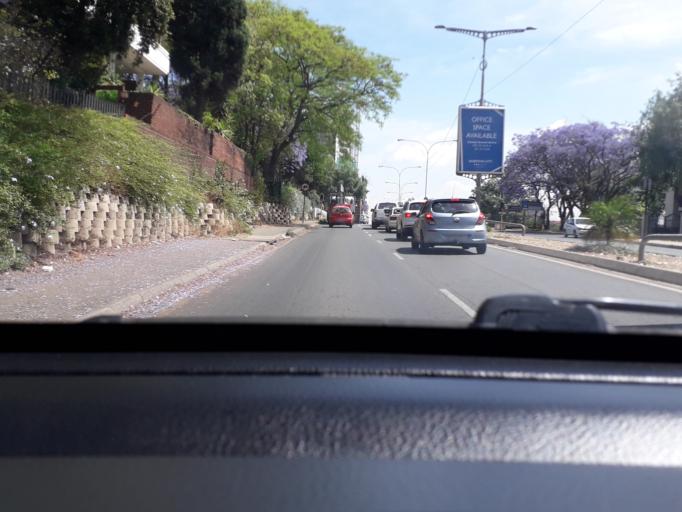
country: ZA
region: Gauteng
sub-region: City of Johannesburg Metropolitan Municipality
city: Johannesburg
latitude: -26.1252
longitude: 28.0487
